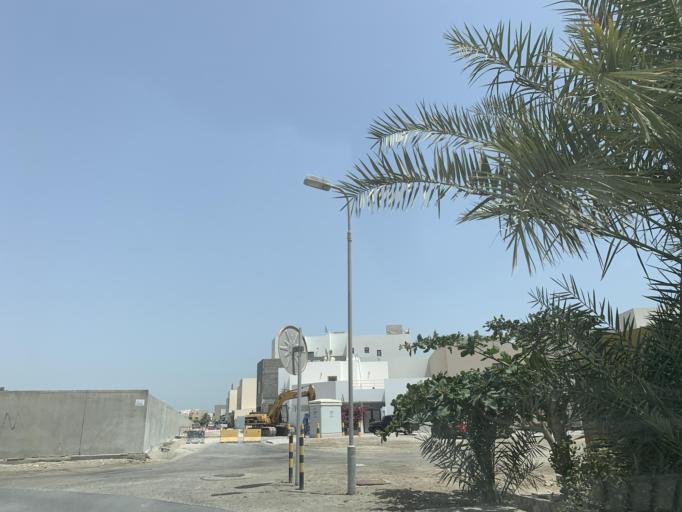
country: BH
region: Northern
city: Madinat `Isa
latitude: 26.1583
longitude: 50.5795
